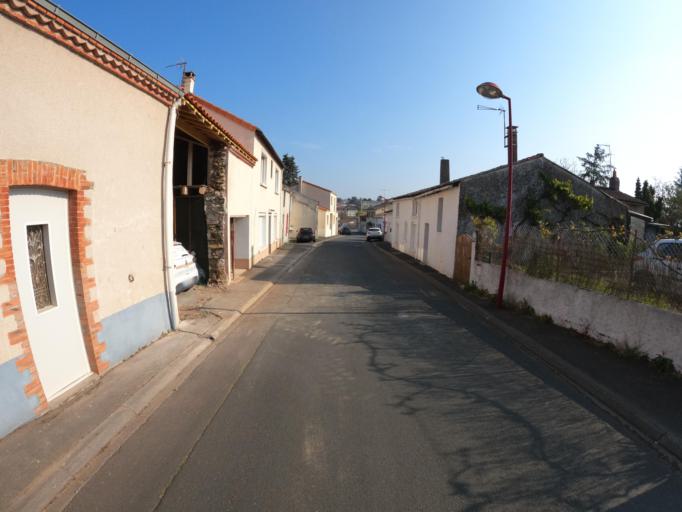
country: FR
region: Pays de la Loire
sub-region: Departement de Maine-et-Loire
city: La Seguiniere
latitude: 47.0590
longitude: -0.9410
